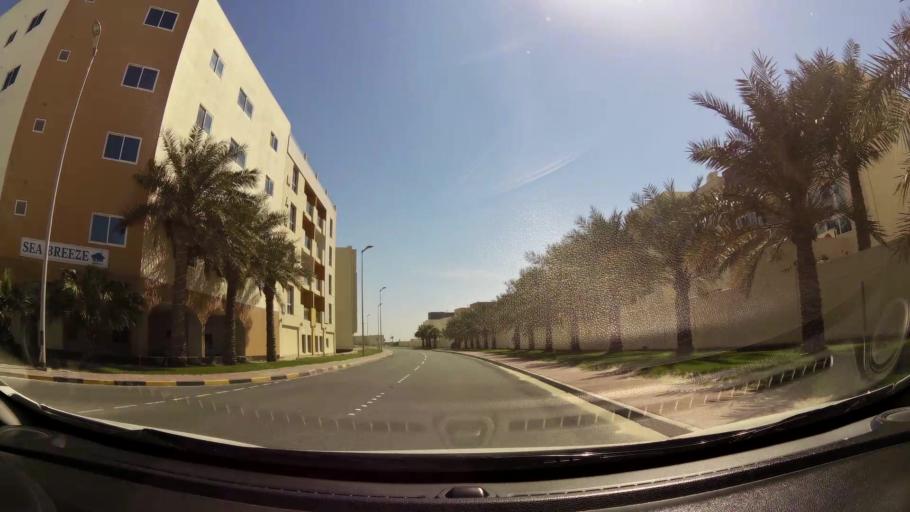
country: BH
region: Muharraq
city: Al Hadd
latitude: 26.2974
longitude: 50.6581
